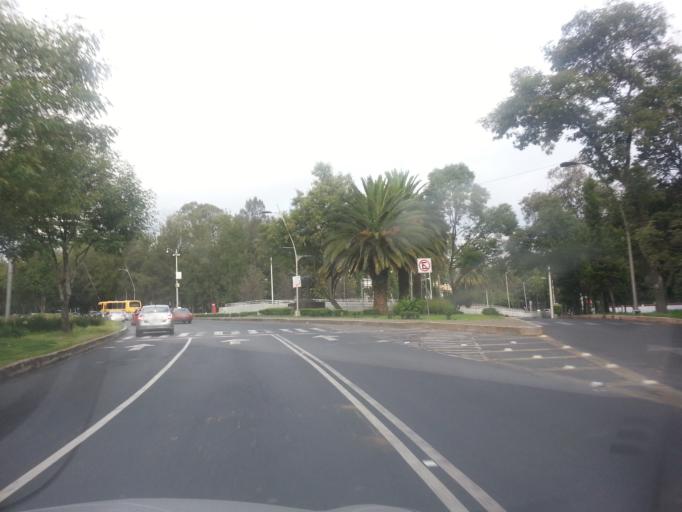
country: MX
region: Mexico City
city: Polanco
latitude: 19.4068
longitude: -99.2269
